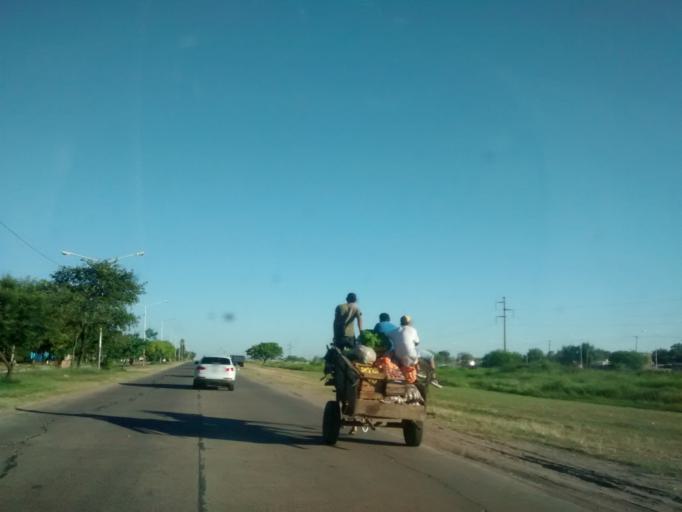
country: AR
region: Chaco
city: Resistencia
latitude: -27.4587
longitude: -59.0212
